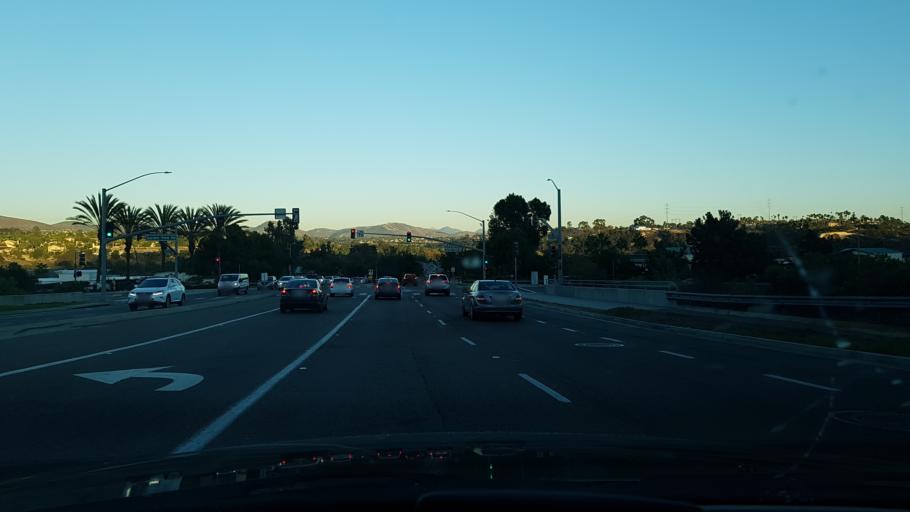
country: US
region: California
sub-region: San Diego County
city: Encinitas
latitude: 33.0685
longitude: -117.2684
